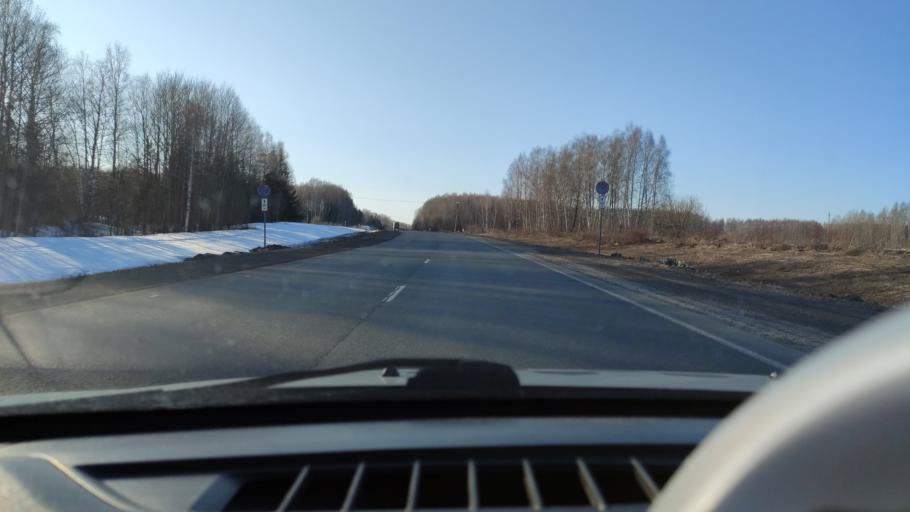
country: RU
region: Perm
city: Suksun
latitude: 57.1536
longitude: 57.2692
